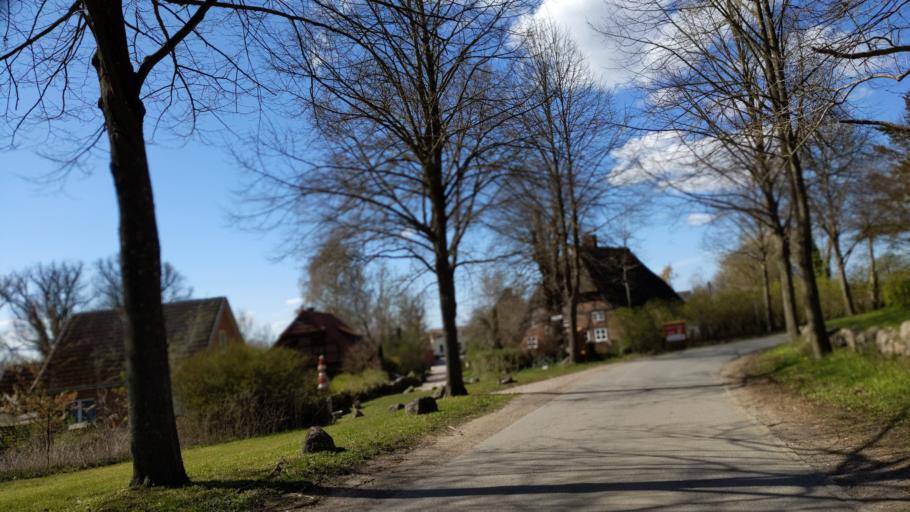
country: DE
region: Schleswig-Holstein
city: Kasseedorf
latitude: 54.1352
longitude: 10.6868
